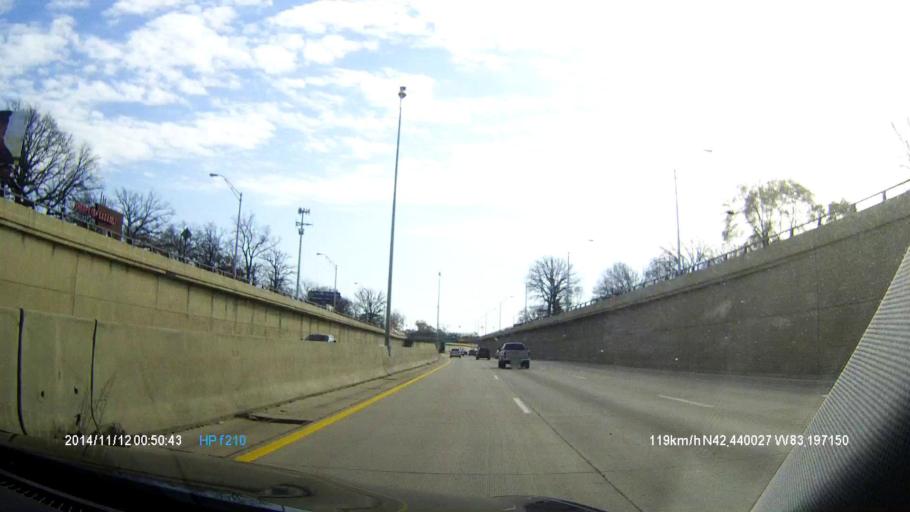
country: US
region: Michigan
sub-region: Oakland County
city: Oak Park
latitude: 42.4397
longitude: -83.1968
